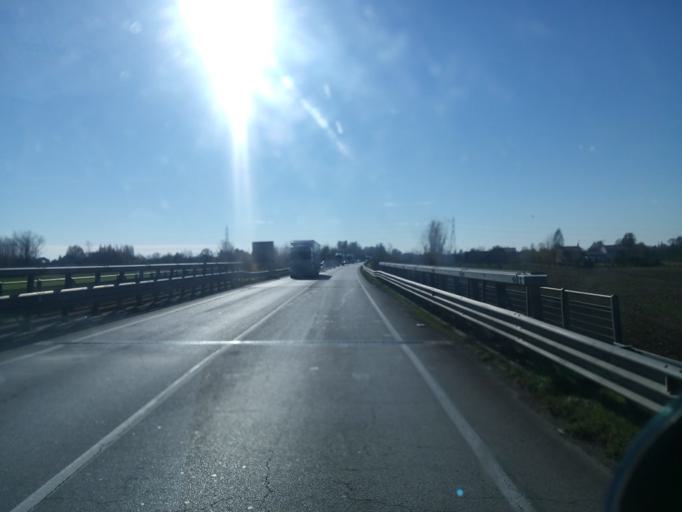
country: IT
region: Veneto
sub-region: Provincia di Padova
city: Loreggia
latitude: 45.5808
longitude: 11.9571
